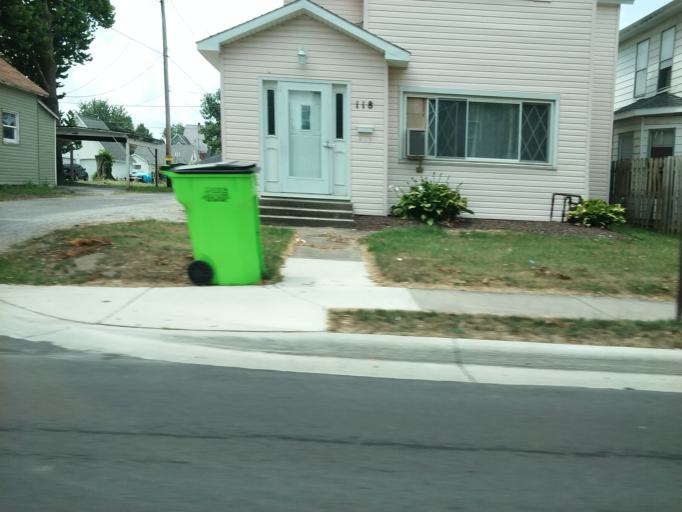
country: US
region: Ohio
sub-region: Hancock County
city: Findlay
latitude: 41.0426
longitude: -83.6598
